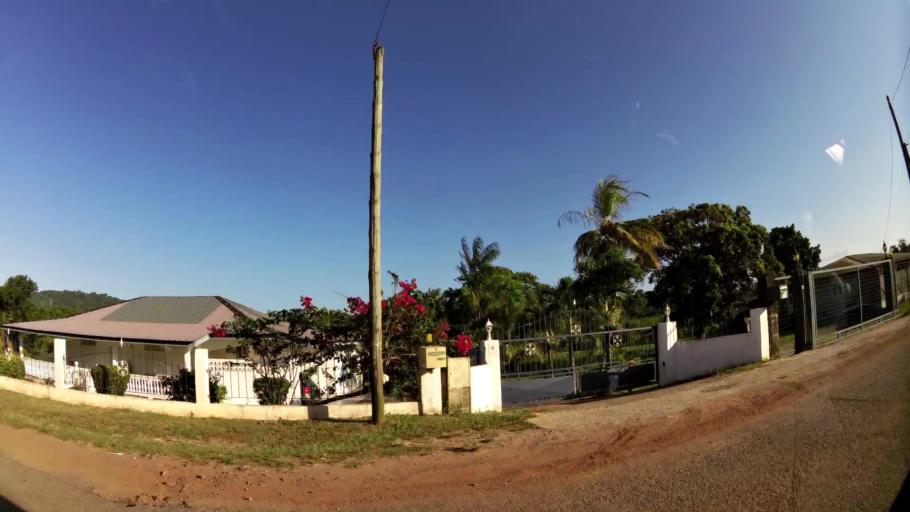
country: GF
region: Guyane
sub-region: Guyane
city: Remire-Montjoly
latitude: 4.8888
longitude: -52.2904
